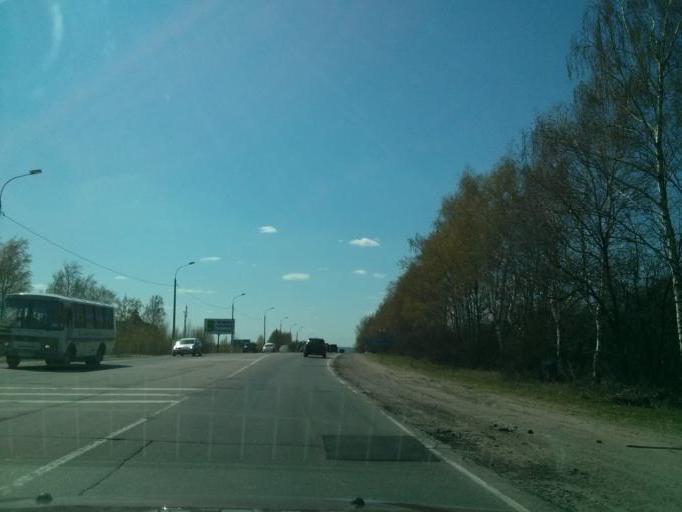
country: RU
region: Nizjnij Novgorod
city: Burevestnik
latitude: 56.1859
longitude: 43.8221
